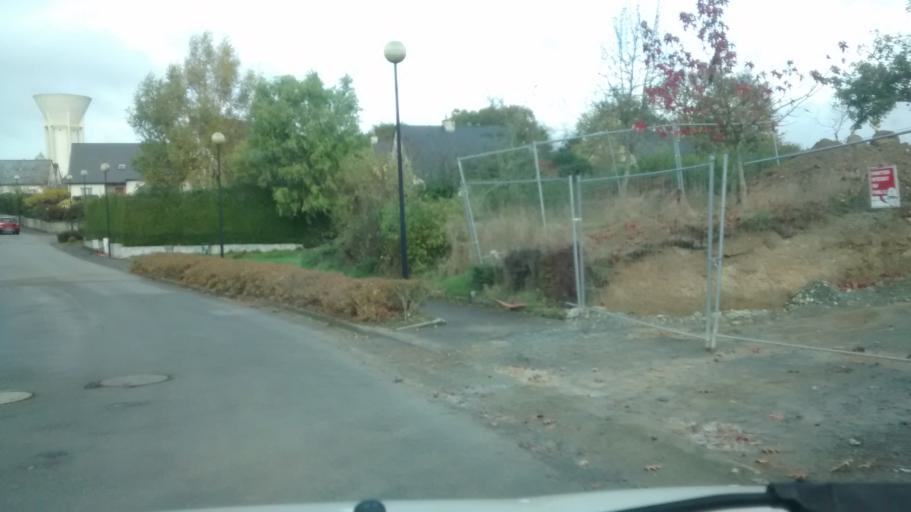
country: FR
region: Brittany
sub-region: Departement d'Ille-et-Vilaine
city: Chateaubourg
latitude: 48.1145
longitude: -1.3941
